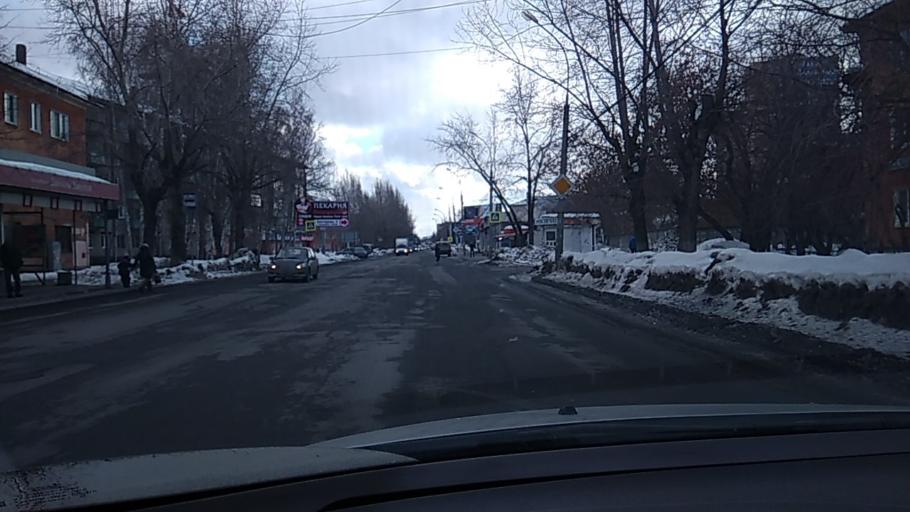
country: RU
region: Sverdlovsk
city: Yekaterinburg
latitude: 56.8641
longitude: 60.6530
